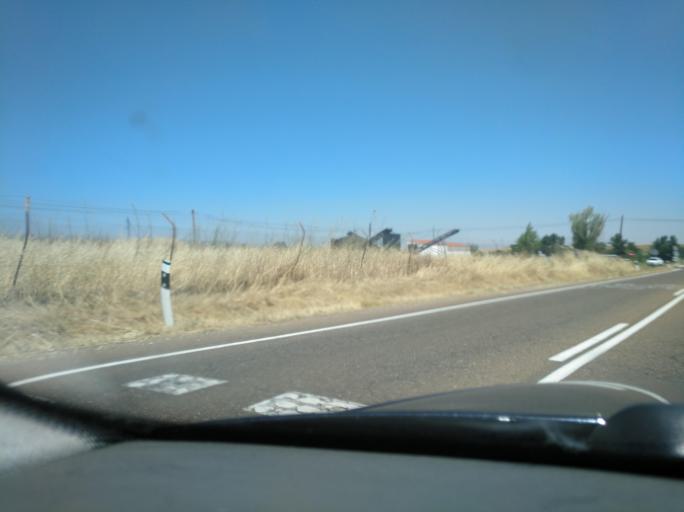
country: ES
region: Extremadura
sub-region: Provincia de Badajoz
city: Olivenza
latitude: 38.7385
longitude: -7.0659
